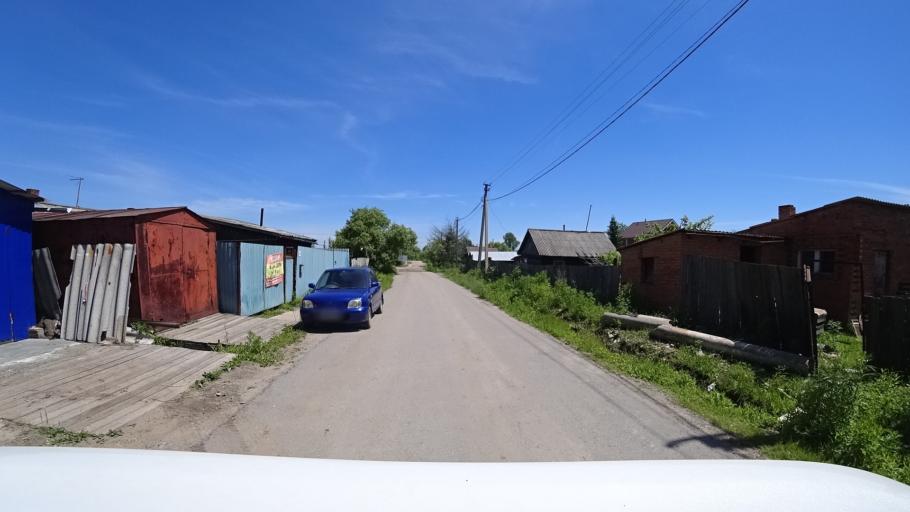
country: RU
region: Khabarovsk Krai
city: Topolevo
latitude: 48.5097
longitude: 135.1839
